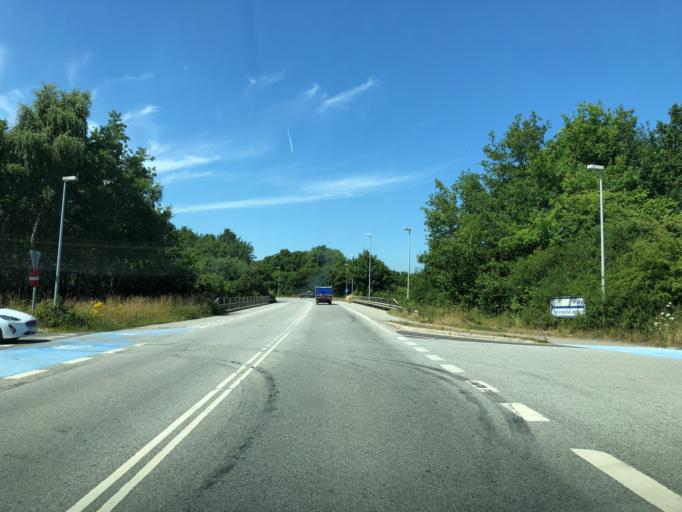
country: DK
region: South Denmark
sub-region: Sonderborg Kommune
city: Sonderborg
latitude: 54.9243
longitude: 9.7823
